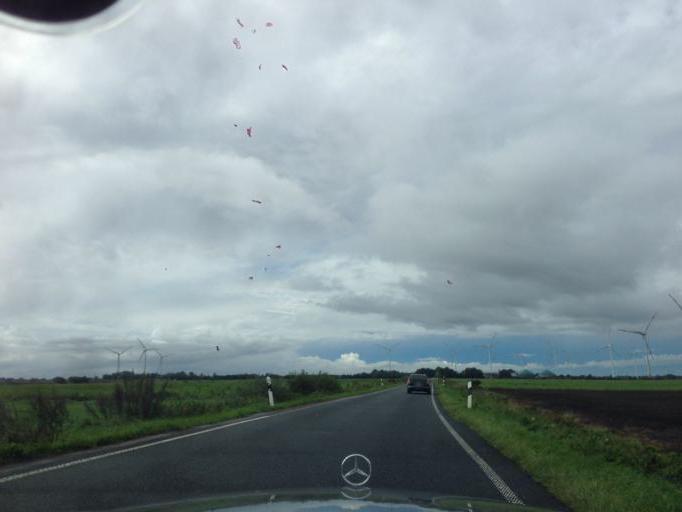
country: DE
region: Schleswig-Holstein
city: Leck
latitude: 54.7750
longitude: 8.9447
